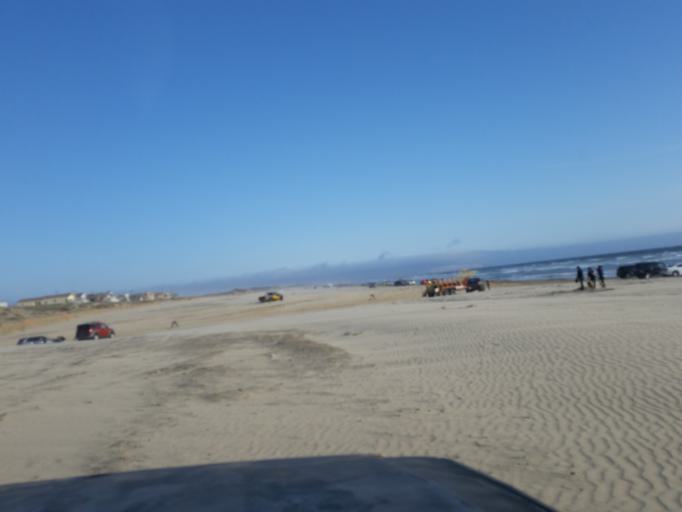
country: US
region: California
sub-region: San Luis Obispo County
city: Grover Beach
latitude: 35.1060
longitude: -120.6316
